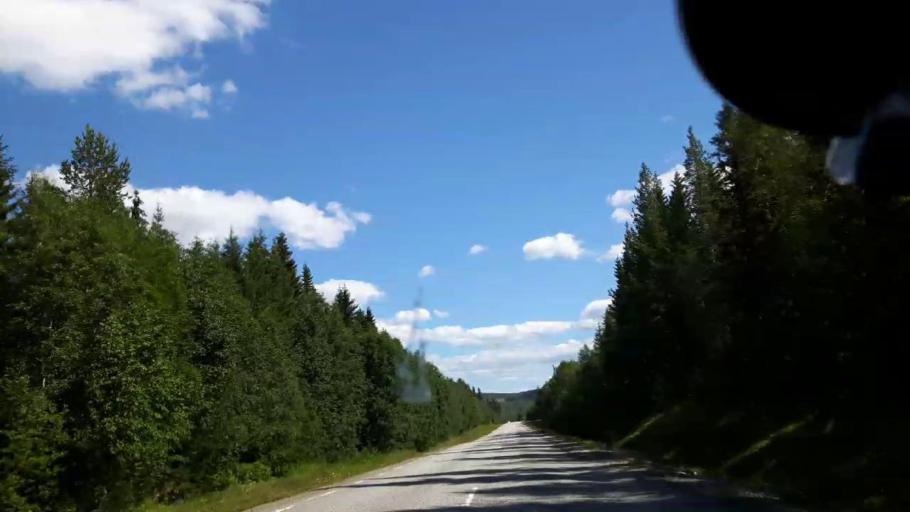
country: SE
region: Jaemtland
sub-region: Ragunda Kommun
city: Hammarstrand
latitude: 62.9613
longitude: 16.1709
